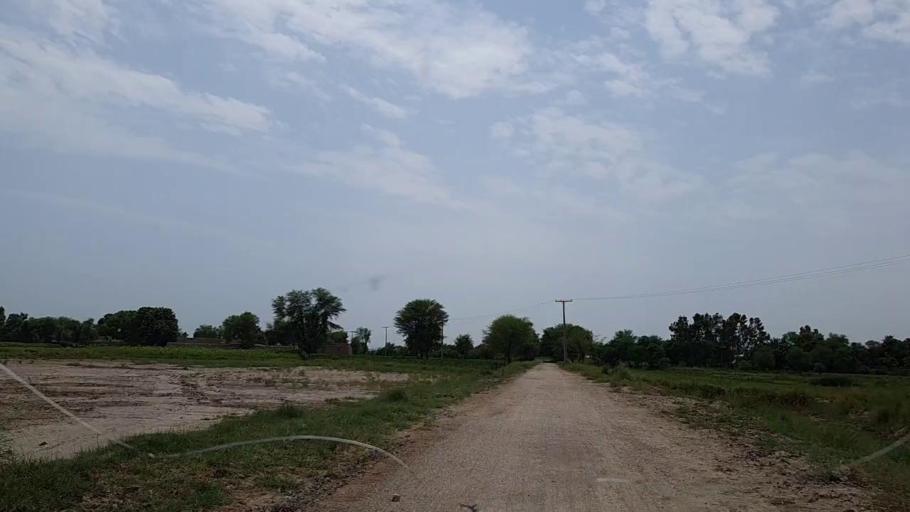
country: PK
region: Sindh
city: Tharu Shah
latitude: 26.9223
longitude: 68.0819
